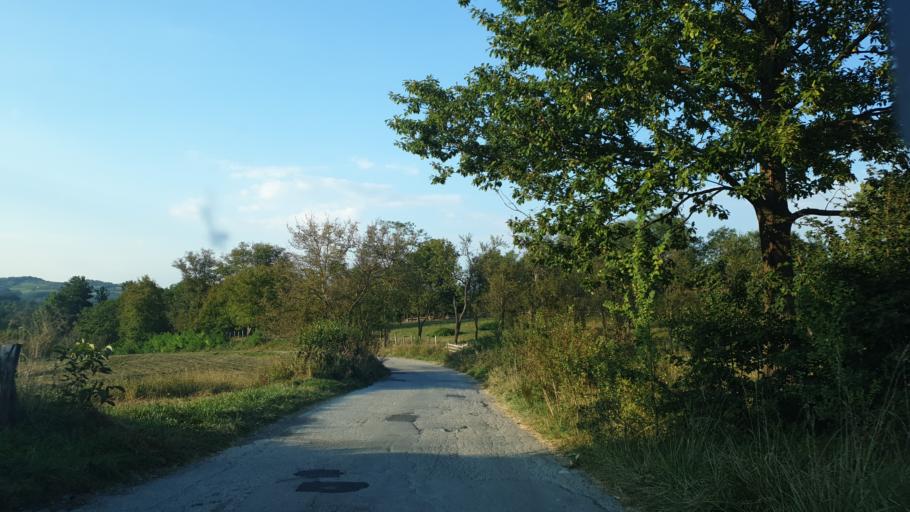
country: RS
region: Central Serbia
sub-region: Zlatiborski Okrug
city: Pozega
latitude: 43.9676
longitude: 20.0239
